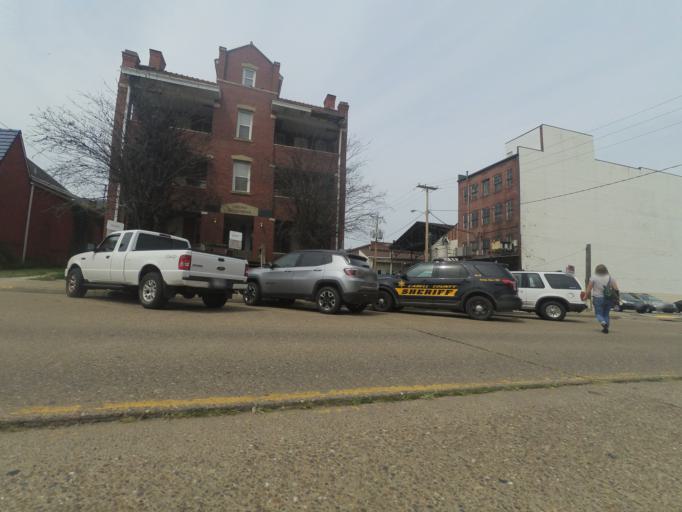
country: US
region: West Virginia
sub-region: Cabell County
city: Huntington
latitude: 38.4193
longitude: -82.4470
